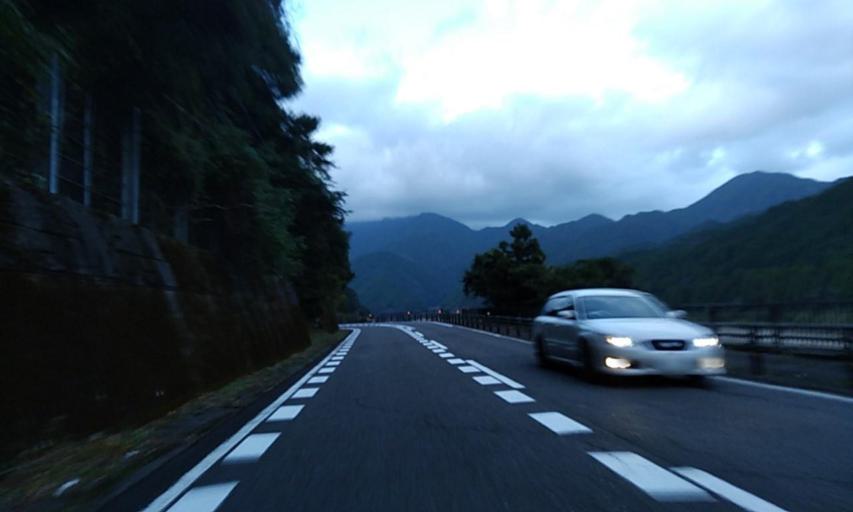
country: JP
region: Wakayama
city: Shingu
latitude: 33.7417
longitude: 135.9386
